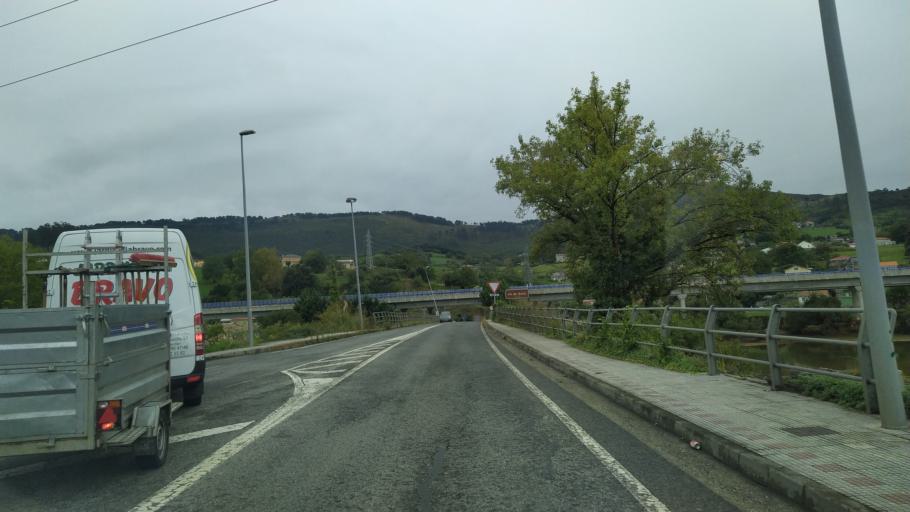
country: ES
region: Cantabria
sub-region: Provincia de Cantabria
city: El Astillero
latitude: 43.3931
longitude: -3.8152
